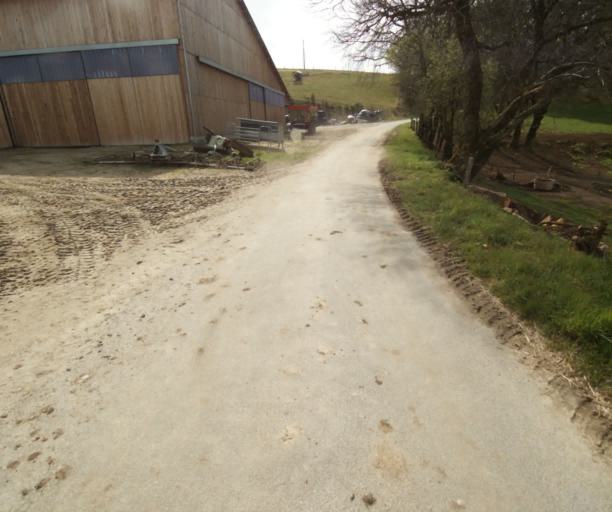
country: FR
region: Limousin
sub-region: Departement de la Correze
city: Correze
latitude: 45.3638
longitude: 1.9078
